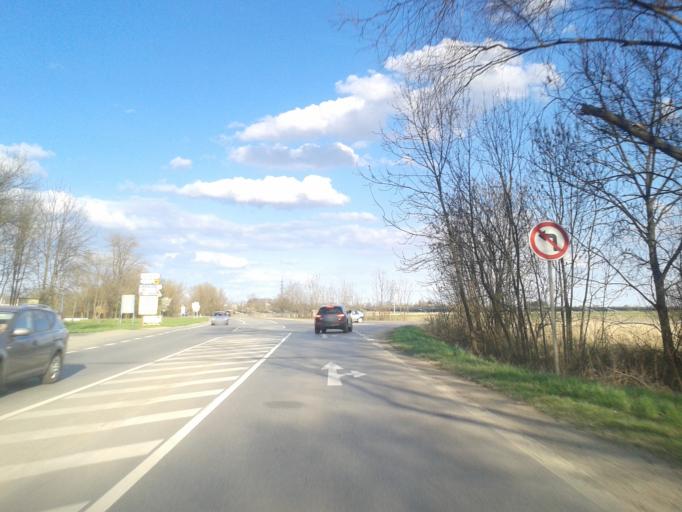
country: CZ
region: Central Bohemia
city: Rudna
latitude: 50.0423
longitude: 14.2600
